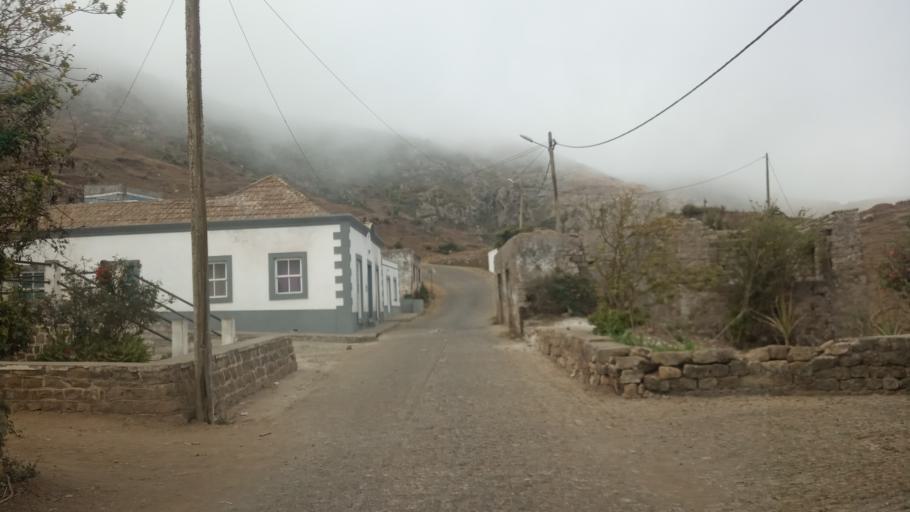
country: CV
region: Brava
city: Vila Nova Sintra
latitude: 14.8697
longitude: -24.7060
